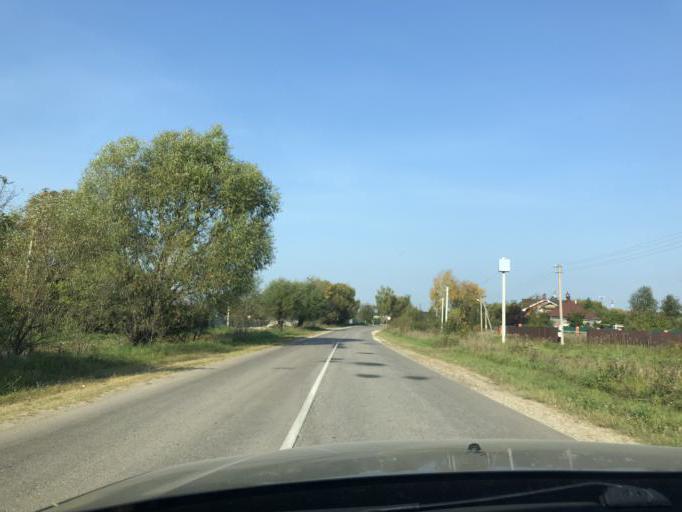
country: RU
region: Tula
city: Leninskiy
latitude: 54.3403
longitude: 37.3712
